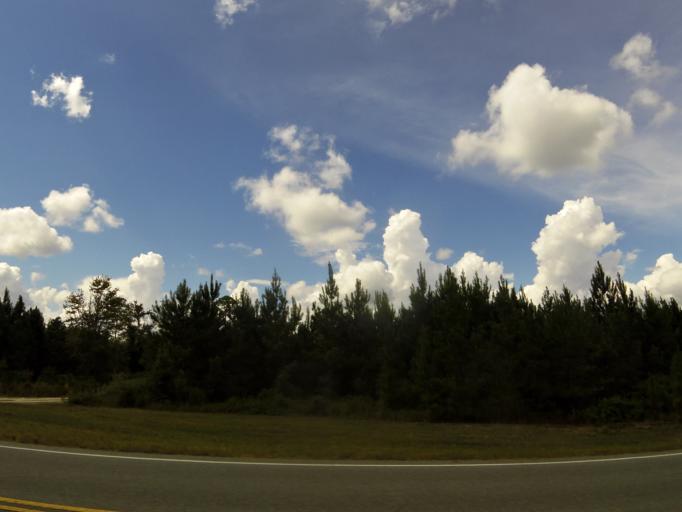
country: US
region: Georgia
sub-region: Brantley County
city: Nahunta
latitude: 31.0866
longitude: -82.0086
